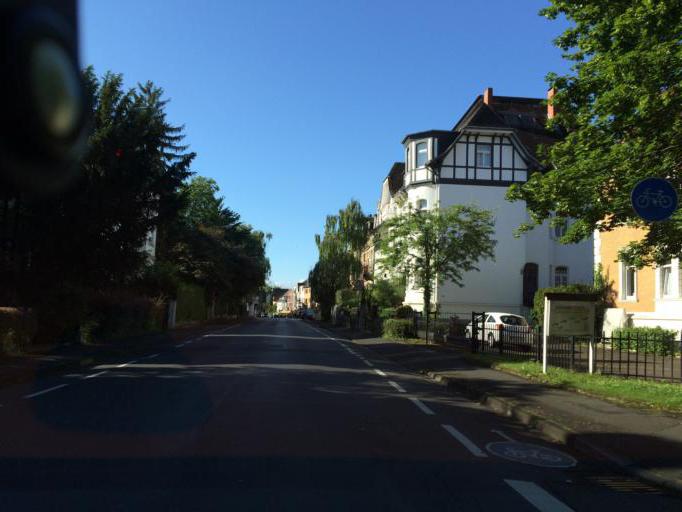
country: DE
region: North Rhine-Westphalia
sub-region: Regierungsbezirk Koln
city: Konigswinter
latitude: 50.6859
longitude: 7.1688
